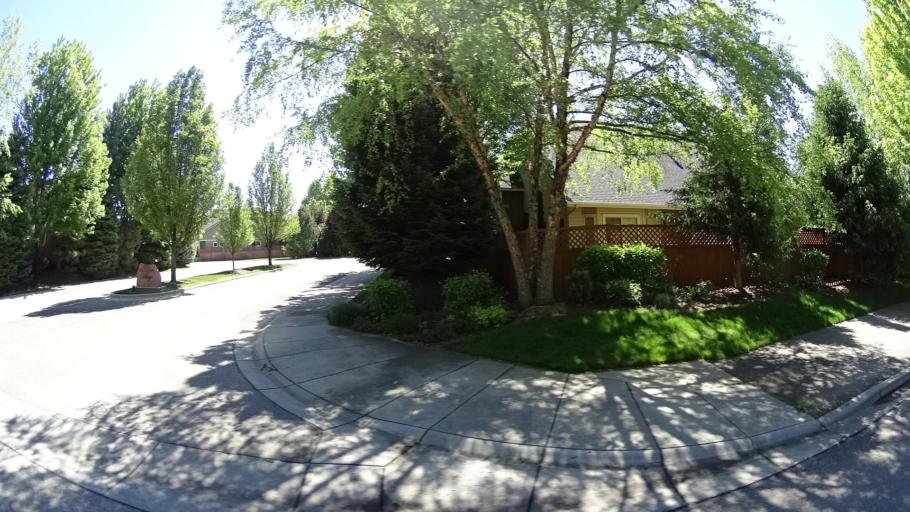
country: US
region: Idaho
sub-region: Ada County
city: Meridian
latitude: 43.6347
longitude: -116.3642
